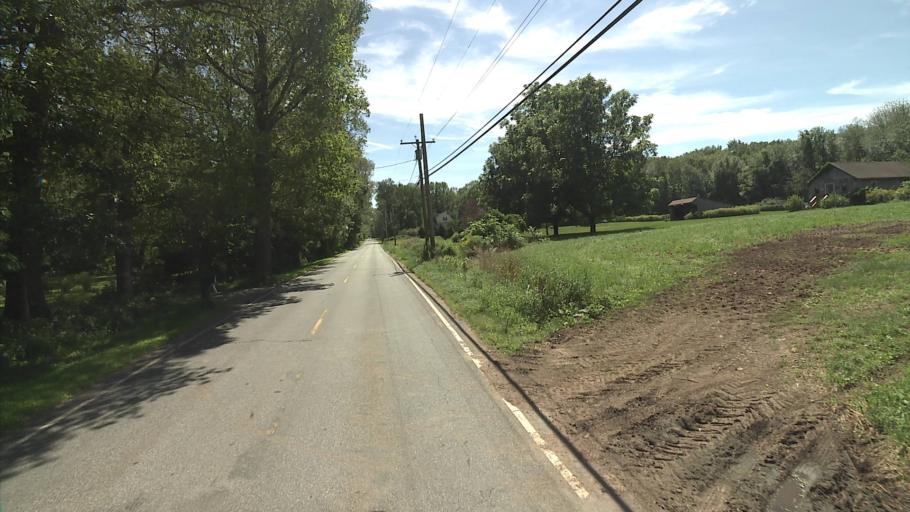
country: US
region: Connecticut
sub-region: Windham County
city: South Woodstock
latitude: 41.8903
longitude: -71.9757
